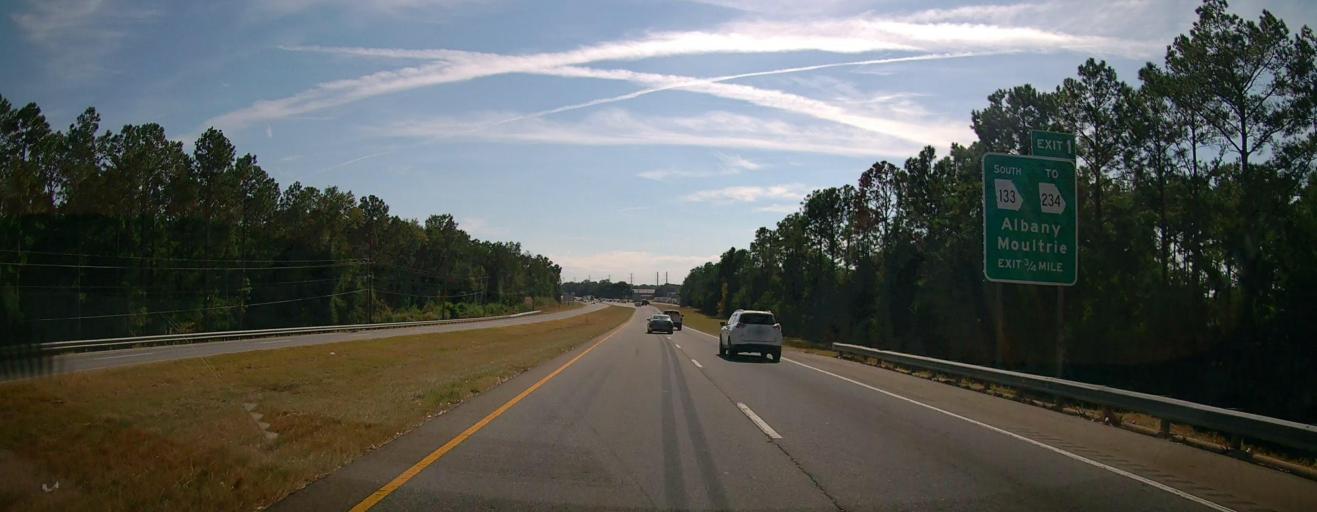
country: US
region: Georgia
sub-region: Dougherty County
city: Albany
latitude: 31.5616
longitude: -84.1140
